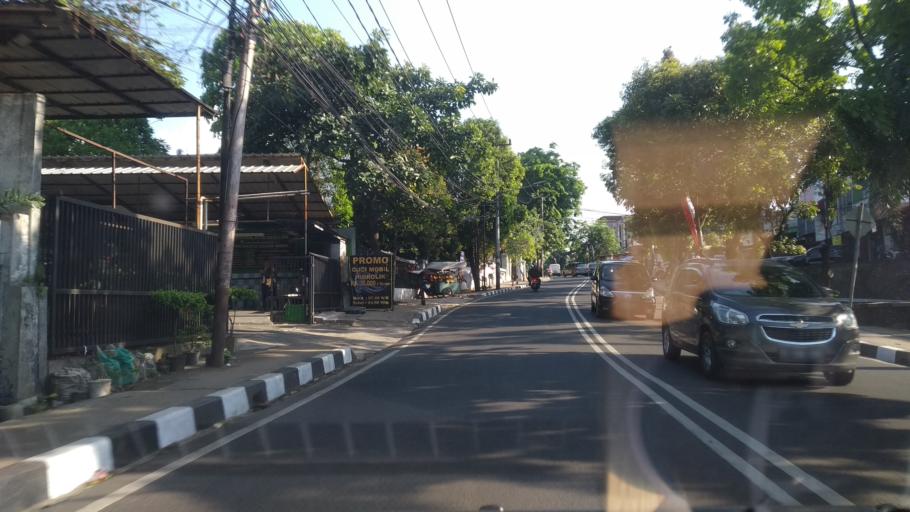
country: ID
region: Banten
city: South Tangerang
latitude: -6.2552
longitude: 106.7691
